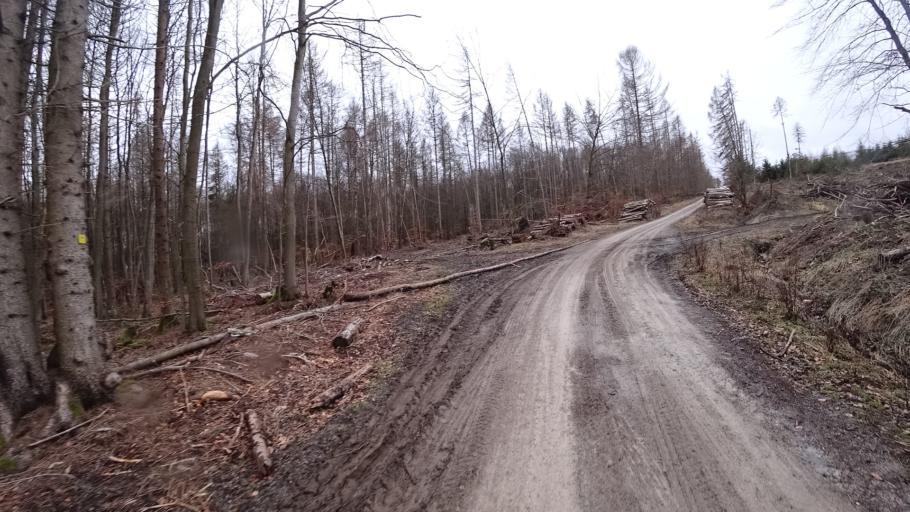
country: DE
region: Rheinland-Pfalz
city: Dernbach
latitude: 50.4333
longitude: 7.7705
